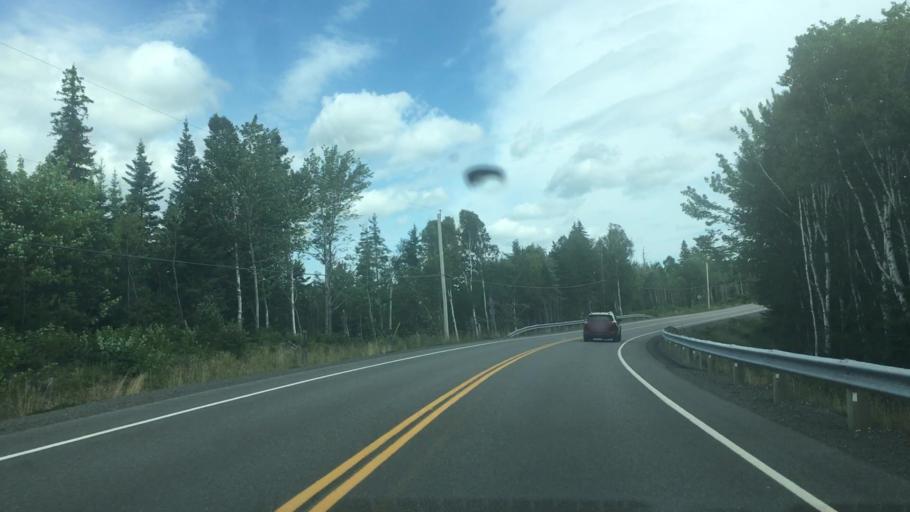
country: CA
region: Nova Scotia
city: Sydney Mines
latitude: 46.3098
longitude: -60.6165
